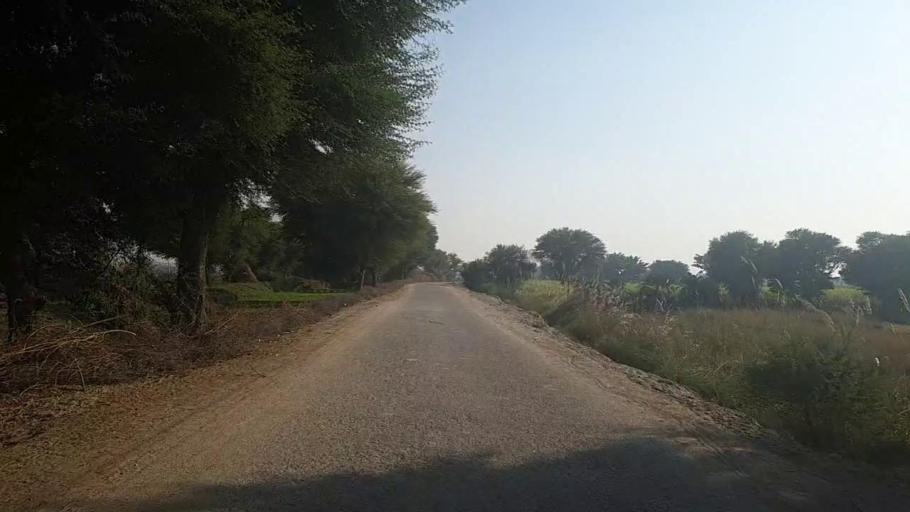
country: PK
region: Sindh
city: Kot Diji
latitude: 27.2663
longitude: 68.6745
